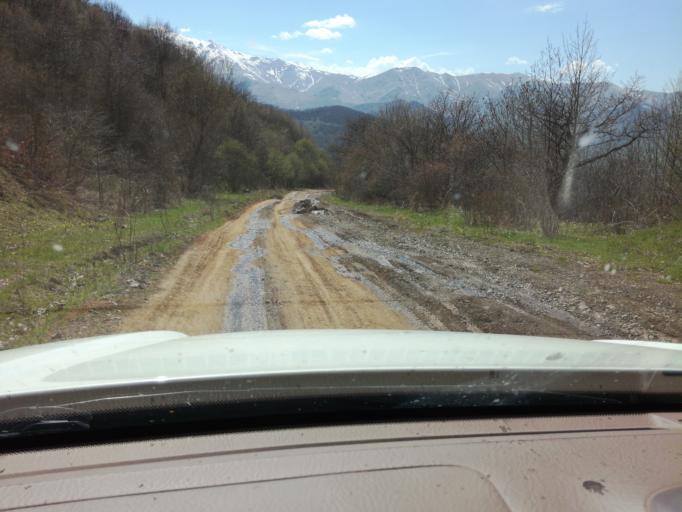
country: AM
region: Syunik'i Marz
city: Shinuhayr
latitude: 39.3641
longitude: 46.2767
